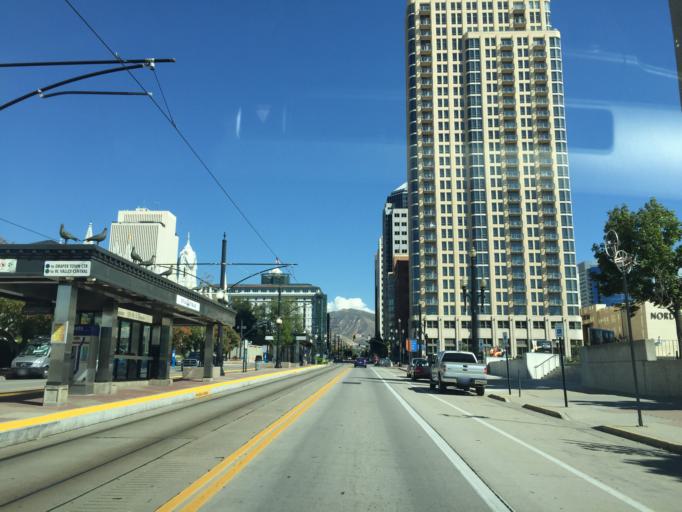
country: US
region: Utah
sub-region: Salt Lake County
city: Salt Lake City
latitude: 40.7692
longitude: -111.8953
